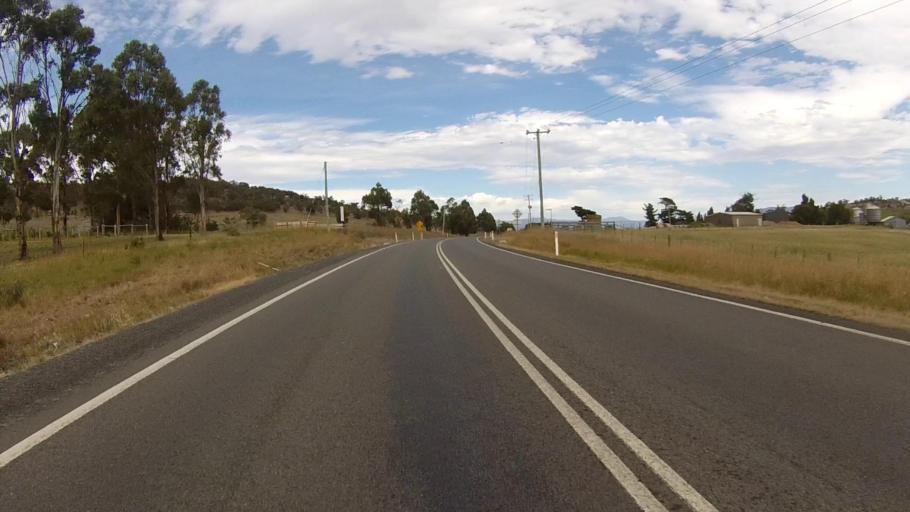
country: AU
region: Tasmania
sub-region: Brighton
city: Old Beach
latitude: -42.6918
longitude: 147.3430
